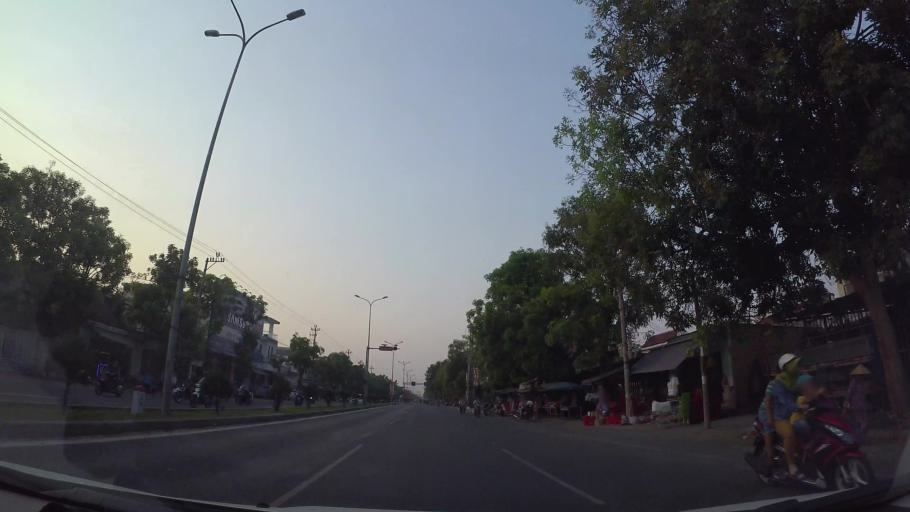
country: VN
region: Quang Nam
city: Quang Nam
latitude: 15.9490
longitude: 108.2196
